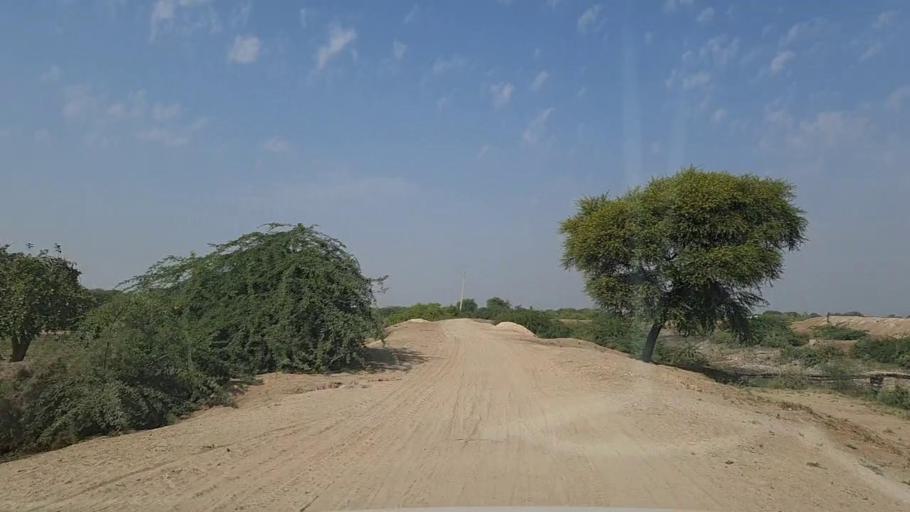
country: PK
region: Sindh
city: Mirpur Batoro
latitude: 24.6753
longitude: 68.3739
